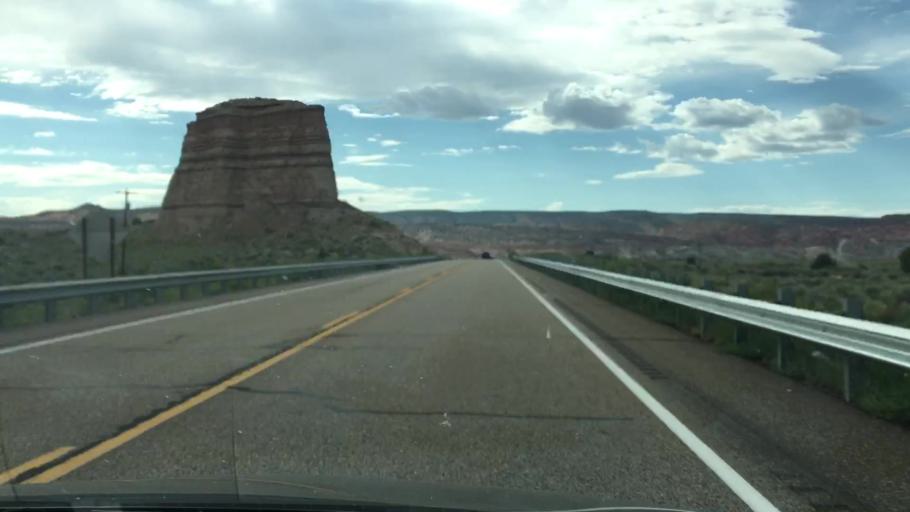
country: US
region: Arizona
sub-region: Coconino County
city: Page
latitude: 37.1097
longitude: -111.9185
